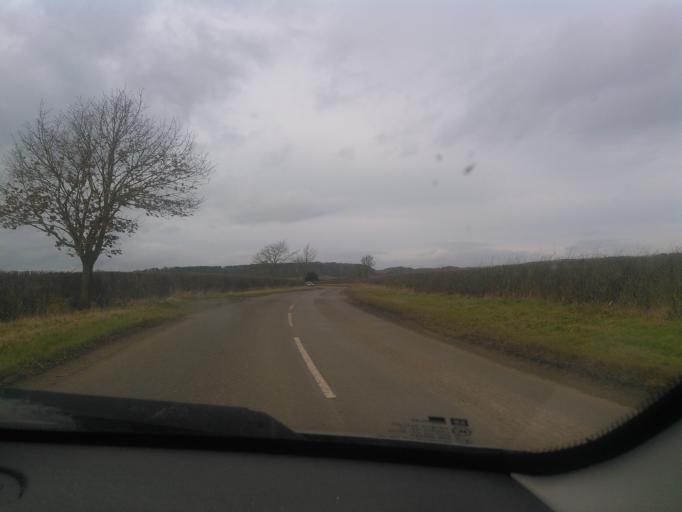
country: GB
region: England
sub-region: Shropshire
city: Shawbury
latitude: 52.8097
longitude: -2.6600
